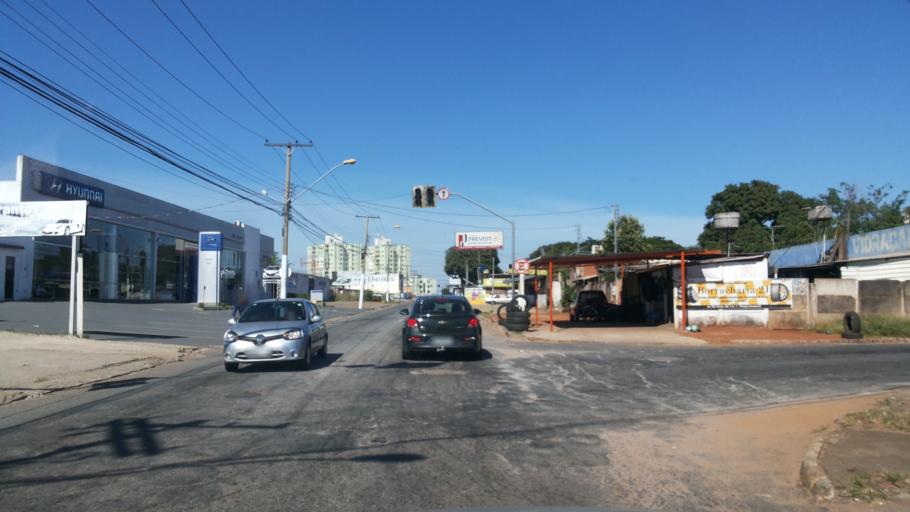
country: BR
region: Goias
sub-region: Goiania
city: Goiania
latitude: -16.7334
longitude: -49.2651
